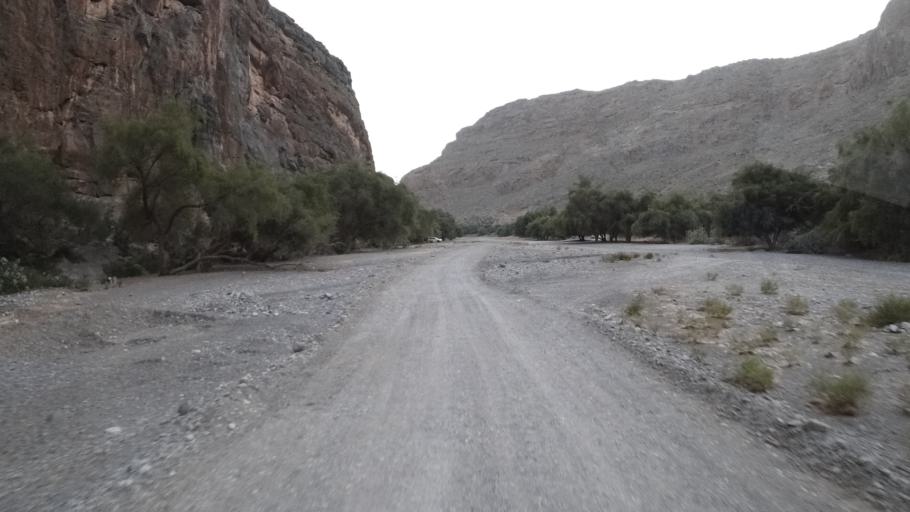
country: OM
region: Muhafazat ad Dakhiliyah
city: Nizwa
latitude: 23.0668
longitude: 57.4718
